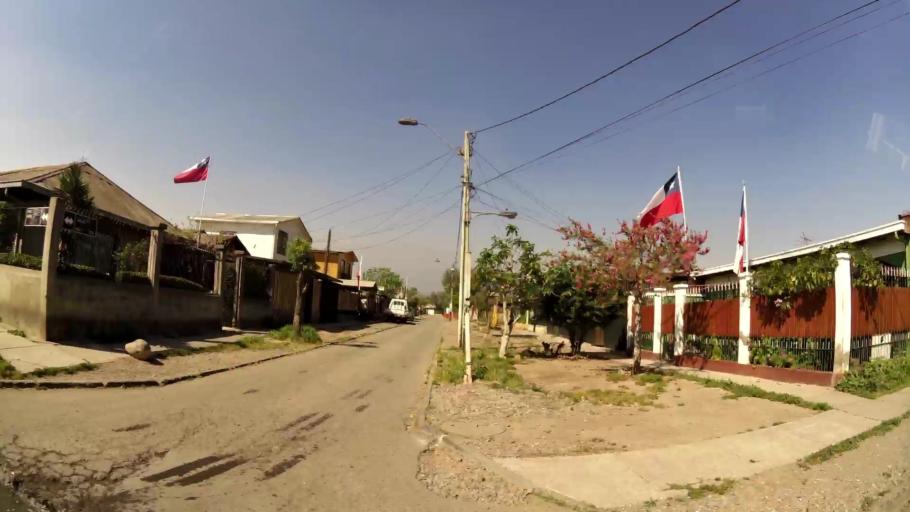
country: CL
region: Santiago Metropolitan
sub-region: Provincia de Santiago
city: La Pintana
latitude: -33.5395
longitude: -70.6097
